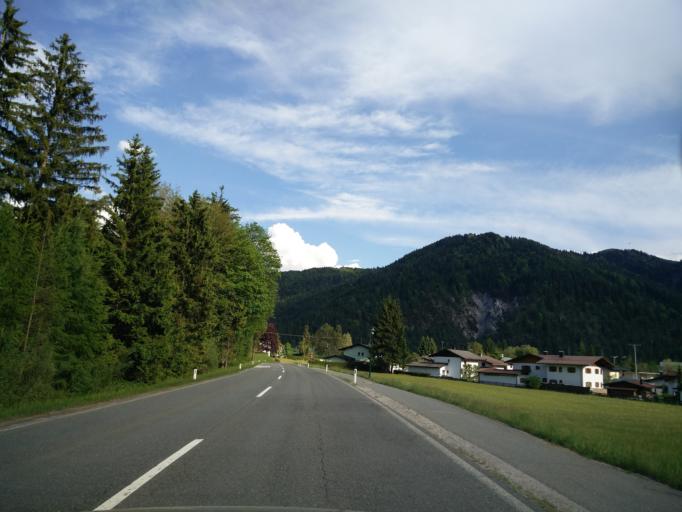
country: AT
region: Tyrol
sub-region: Politischer Bezirk Kitzbuhel
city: Kirchdorf in Tirol
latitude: 47.5829
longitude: 12.4750
